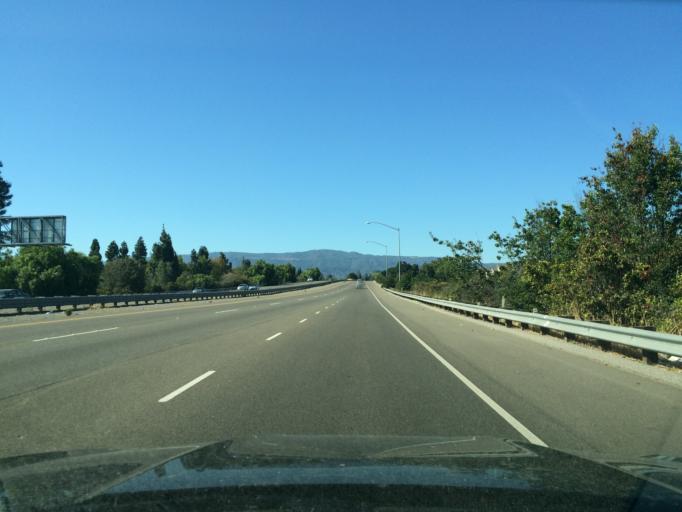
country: US
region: California
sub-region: Santa Clara County
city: Sunnyvale
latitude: 37.3906
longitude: -122.0533
